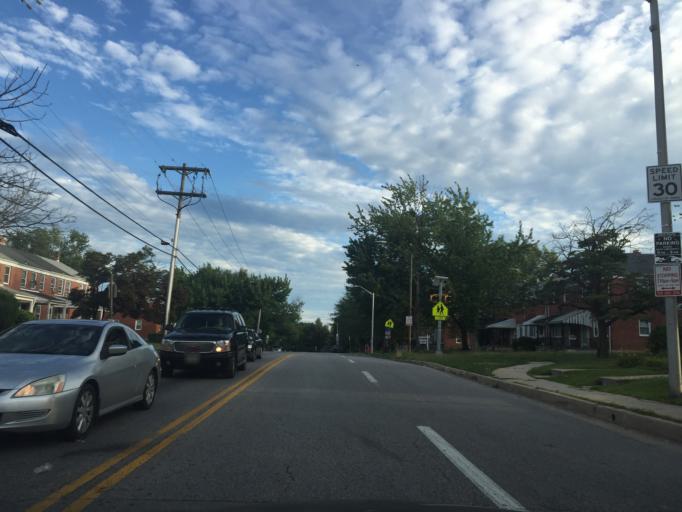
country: US
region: Maryland
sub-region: Baltimore County
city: Towson
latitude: 39.3668
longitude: -76.5934
